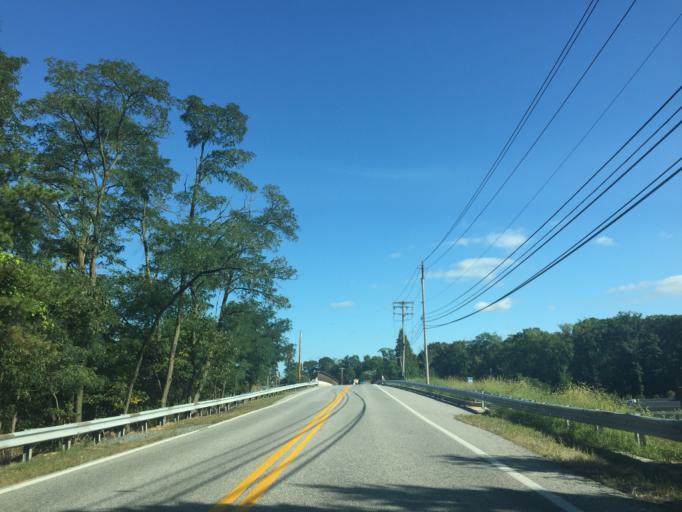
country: US
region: Maryland
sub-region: Baltimore County
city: Rossville
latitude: 39.3603
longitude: -76.4815
